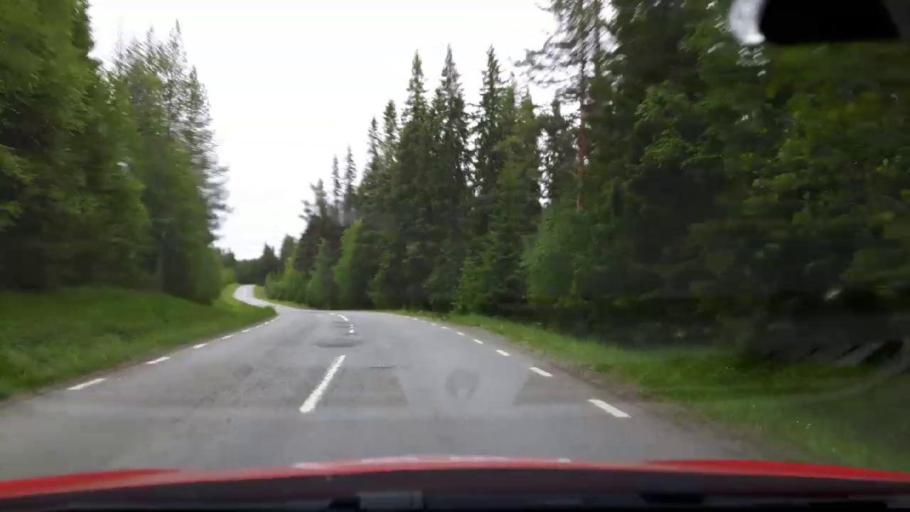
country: SE
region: Jaemtland
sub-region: Stroemsunds Kommun
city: Stroemsund
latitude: 63.4481
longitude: 15.4710
